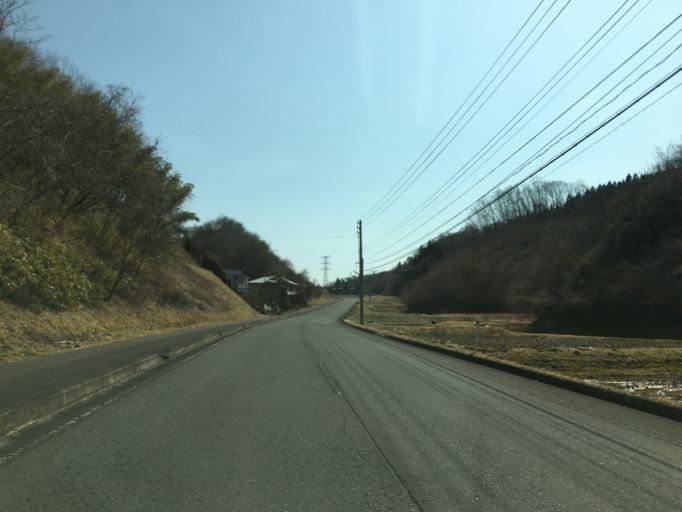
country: JP
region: Fukushima
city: Ishikawa
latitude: 37.0421
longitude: 140.4708
